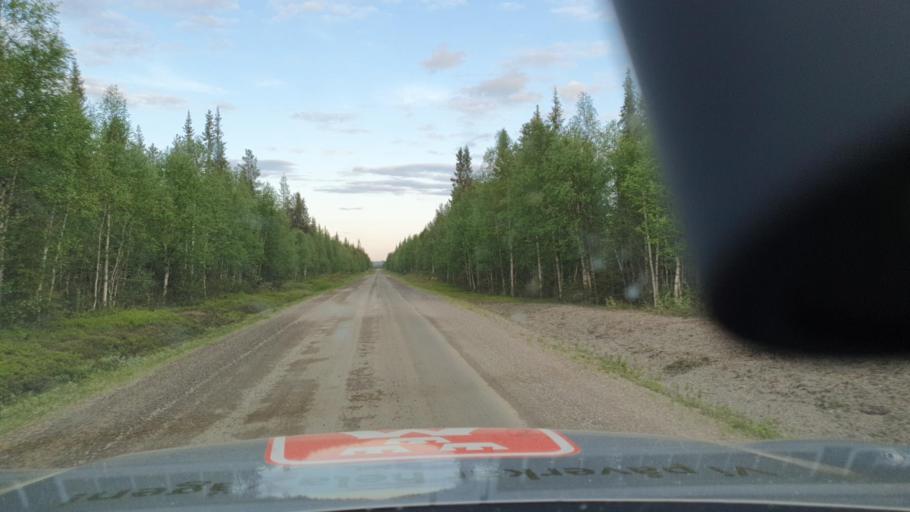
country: SE
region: Norrbotten
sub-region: Bodens Kommun
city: Boden
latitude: 66.5929
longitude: 21.3772
